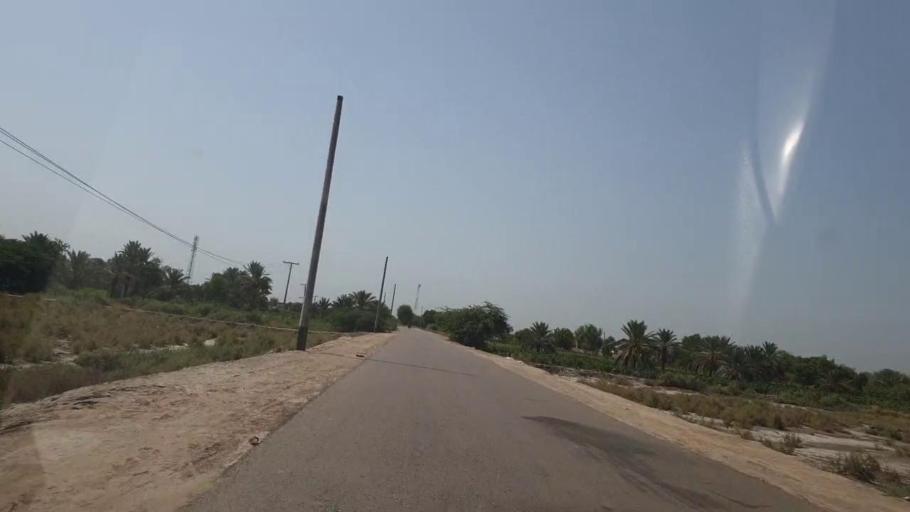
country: PK
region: Sindh
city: Setharja Old
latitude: 27.1264
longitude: 68.5387
